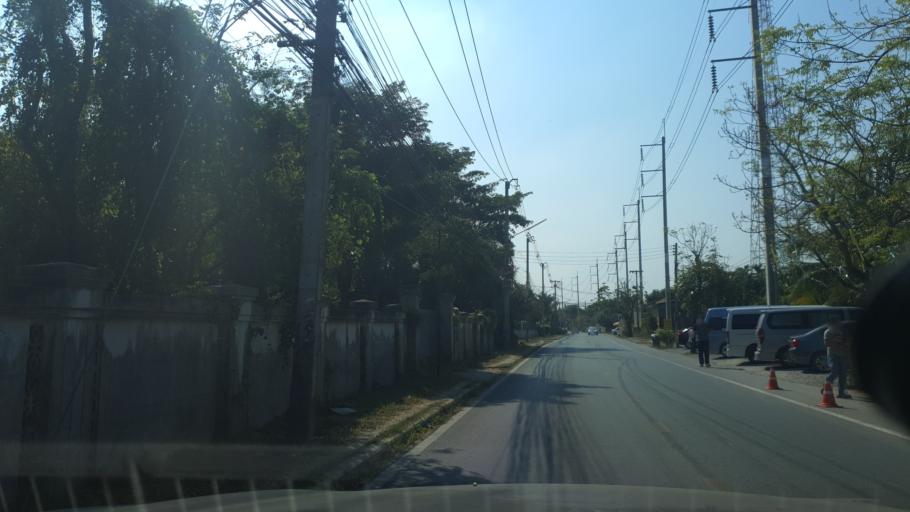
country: TH
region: Nakhon Pathom
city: Salaya
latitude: 13.7833
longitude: 100.2694
